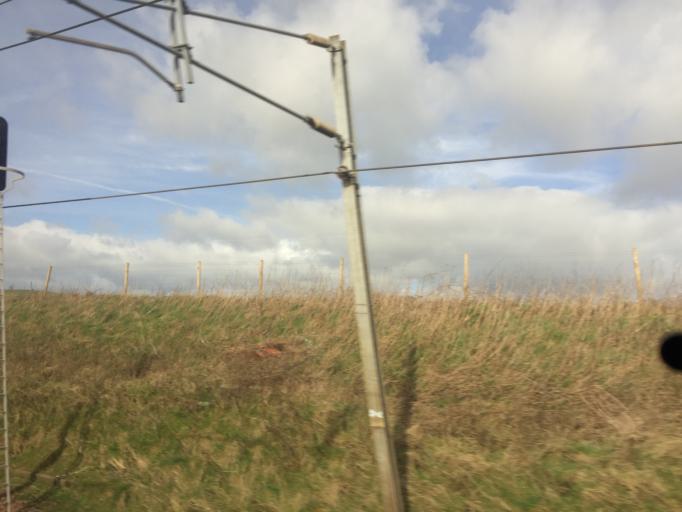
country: GB
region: Scotland
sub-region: Dumfries and Galloway
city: Annan
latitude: 55.0655
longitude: -3.2368
